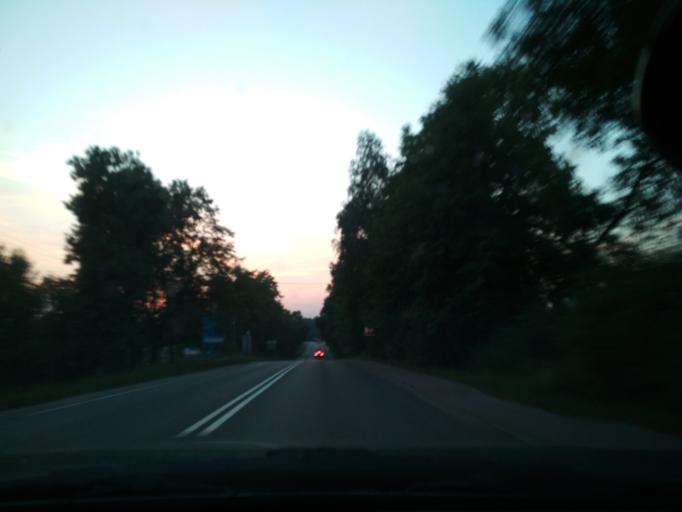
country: PL
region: Silesian Voivodeship
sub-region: Powiat zawiercianski
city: Ogrodzieniec
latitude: 50.4753
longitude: 19.4761
